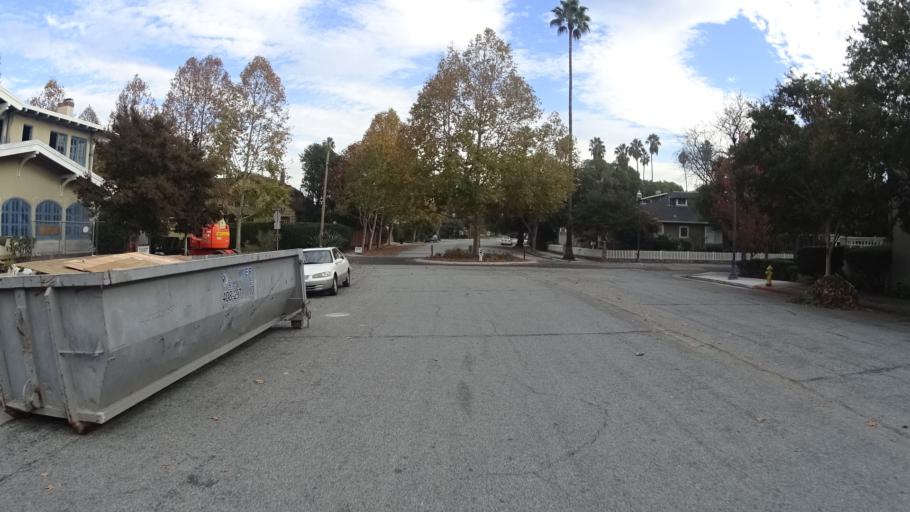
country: US
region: California
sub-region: Santa Clara County
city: Buena Vista
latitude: 37.3302
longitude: -121.9168
